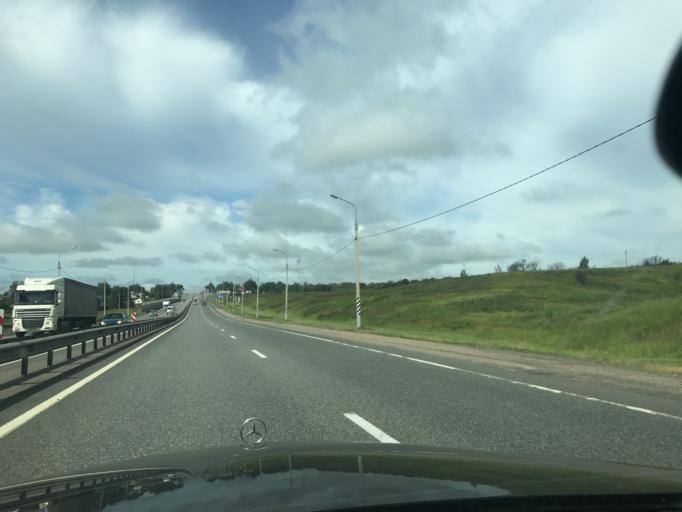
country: RU
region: Smolensk
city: Yartsevo
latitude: 55.0726
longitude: 32.6466
